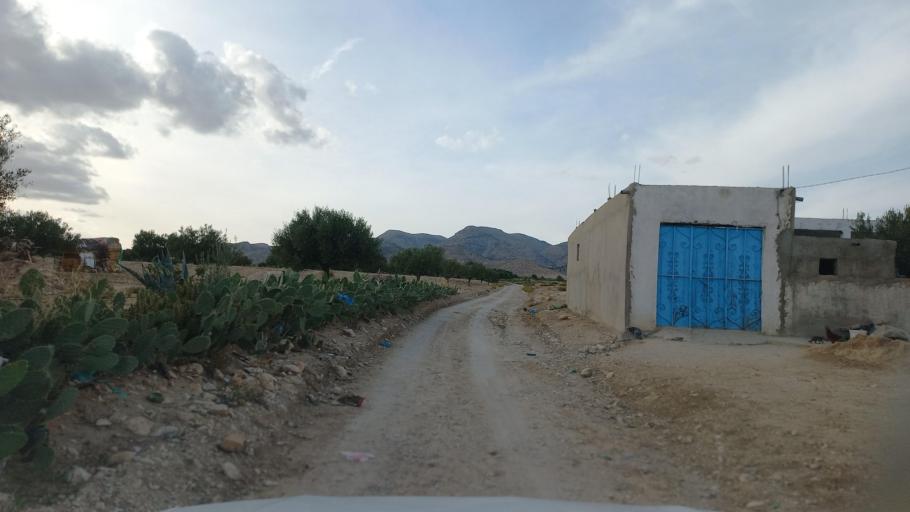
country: TN
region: Al Qasrayn
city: Sbiba
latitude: 35.4426
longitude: 9.0732
